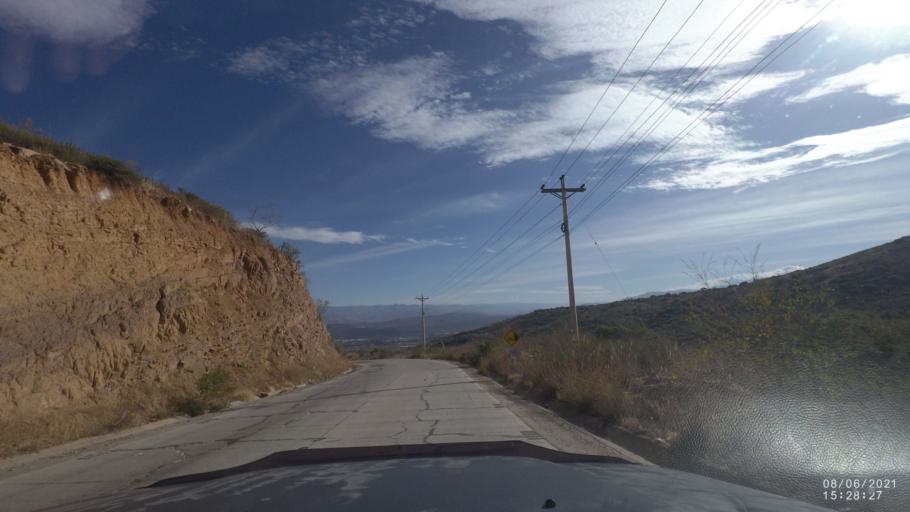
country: BO
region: Cochabamba
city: Cochabamba
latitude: -17.5348
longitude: -66.2067
